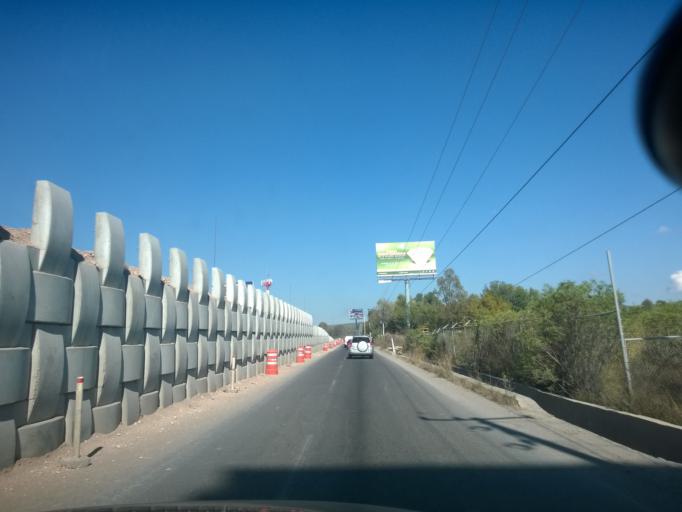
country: MX
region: Guanajuato
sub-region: Leon
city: Fraccionamiento Paseo de las Torres
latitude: 21.1927
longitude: -101.7485
